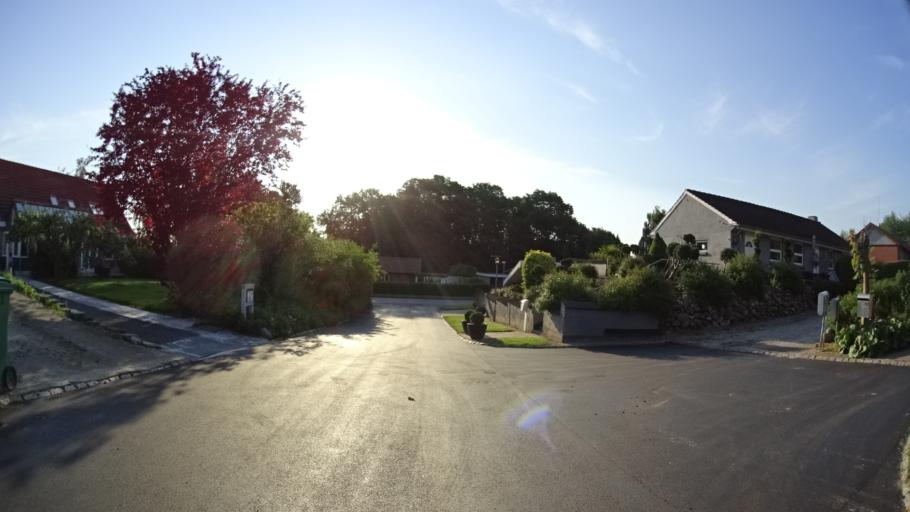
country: DK
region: Central Jutland
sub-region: Arhus Kommune
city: Stavtrup
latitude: 56.1296
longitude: 10.1287
